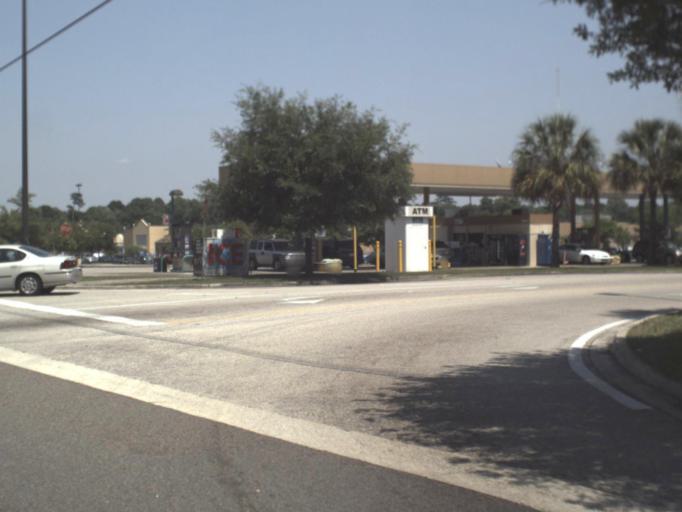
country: US
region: Florida
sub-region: Duval County
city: Jacksonville
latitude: 30.3021
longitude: -81.7615
